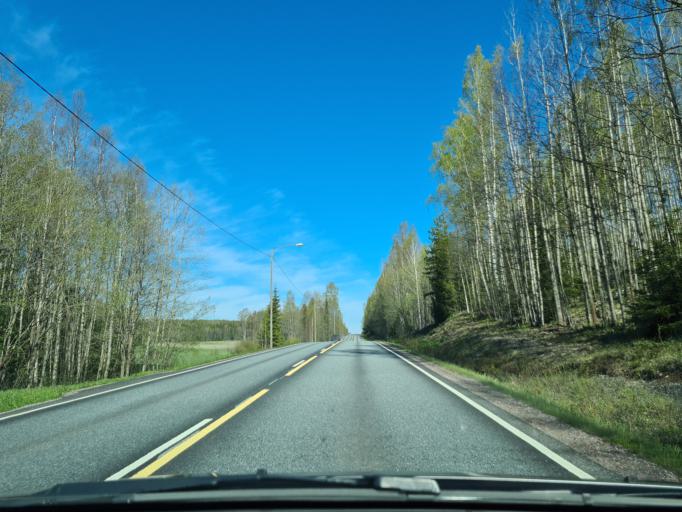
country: FI
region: Uusimaa
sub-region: Helsinki
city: Karkkila
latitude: 60.4998
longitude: 24.2732
